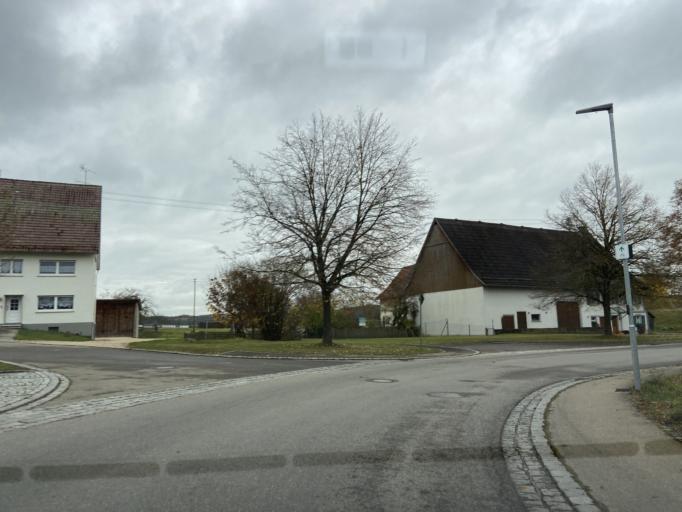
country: DE
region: Baden-Wuerttemberg
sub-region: Tuebingen Region
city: Messkirch
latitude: 48.0080
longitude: 9.1607
